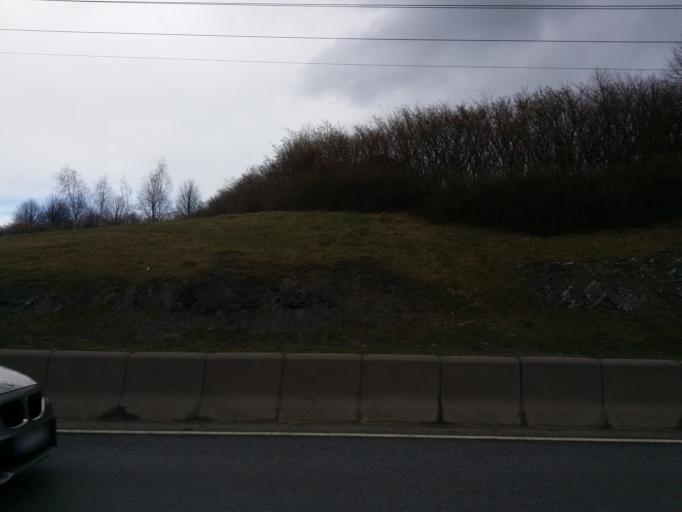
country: NO
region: Oslo
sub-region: Oslo
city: Oslo
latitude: 59.9166
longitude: 10.8126
